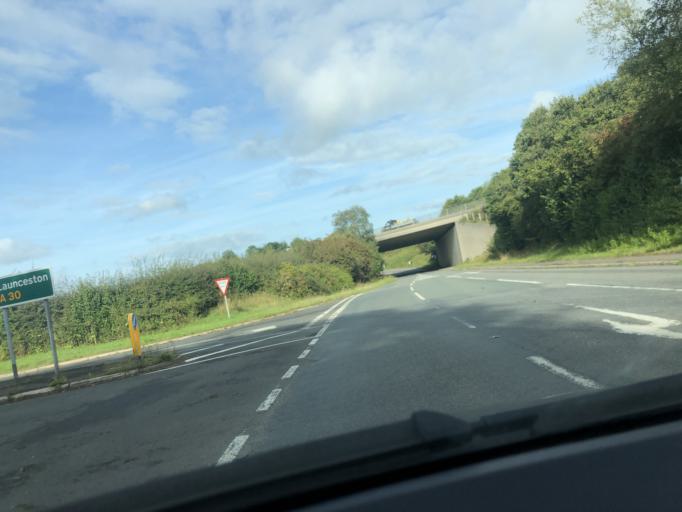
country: GB
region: England
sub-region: Cornwall
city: Launceston
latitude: 50.6453
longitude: -4.3005
